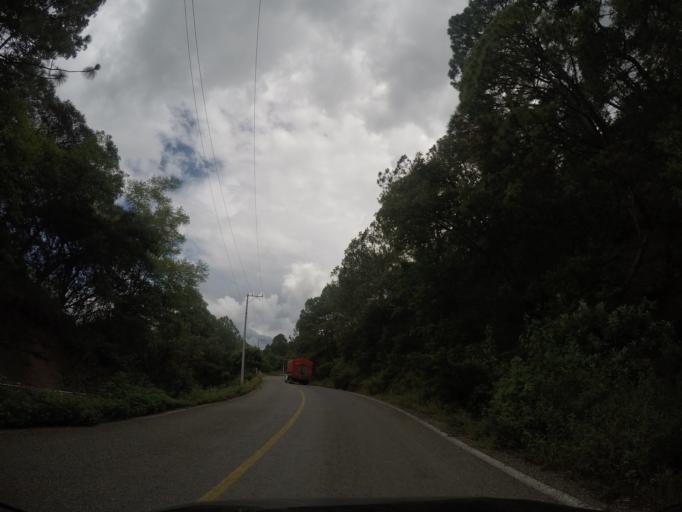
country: MX
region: Oaxaca
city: San Francisco Sola
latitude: 16.4860
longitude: -96.9837
